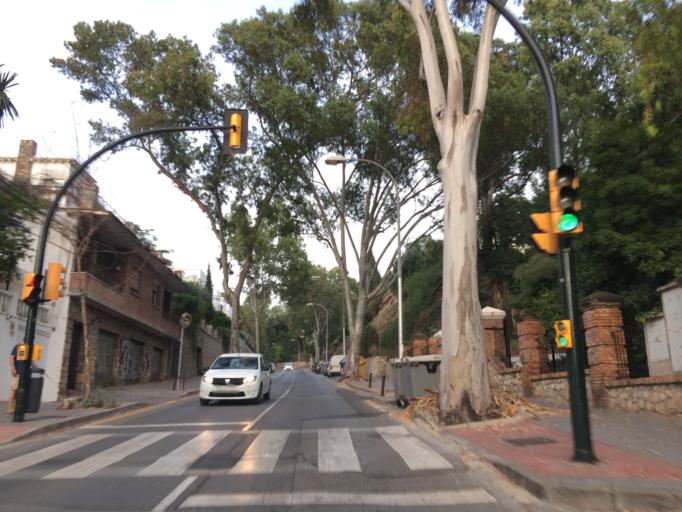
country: ES
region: Andalusia
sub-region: Provincia de Malaga
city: Malaga
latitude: 36.7272
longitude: -4.4086
